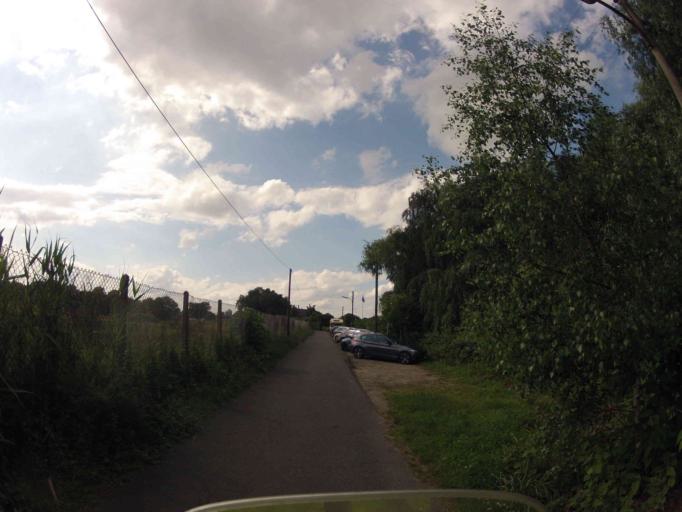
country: DE
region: Hamburg
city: Rothenburgsort
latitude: 53.5268
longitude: 10.0559
